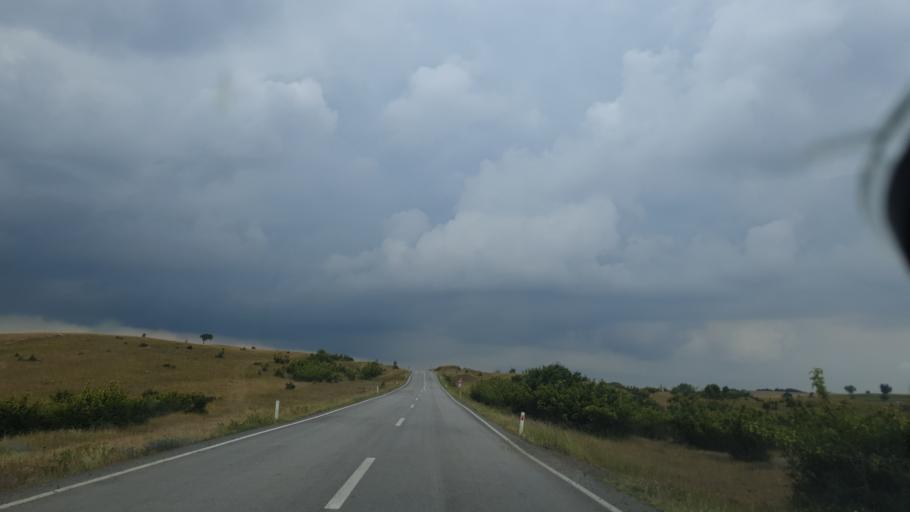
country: TR
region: Tekirdag
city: Hayrabolu
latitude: 41.2218
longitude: 27.0167
